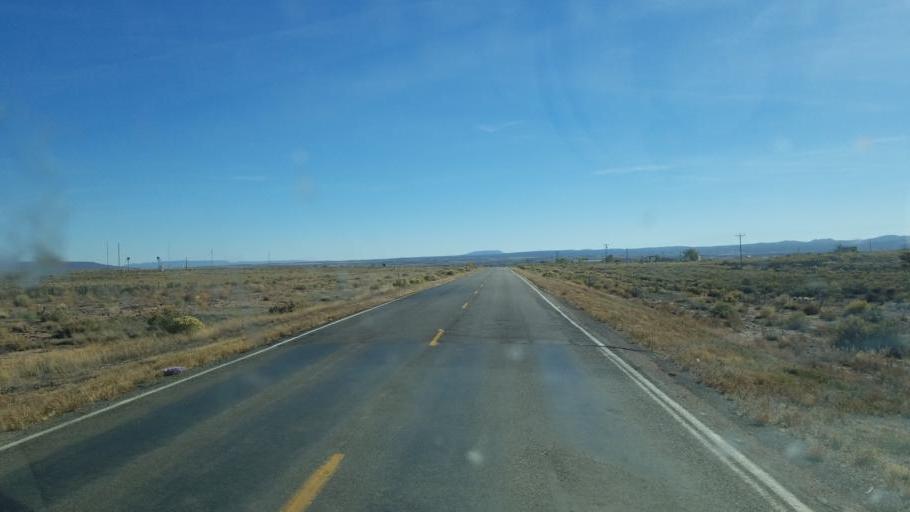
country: US
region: New Mexico
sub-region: Cibola County
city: Milan
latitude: 35.3028
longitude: -107.9877
